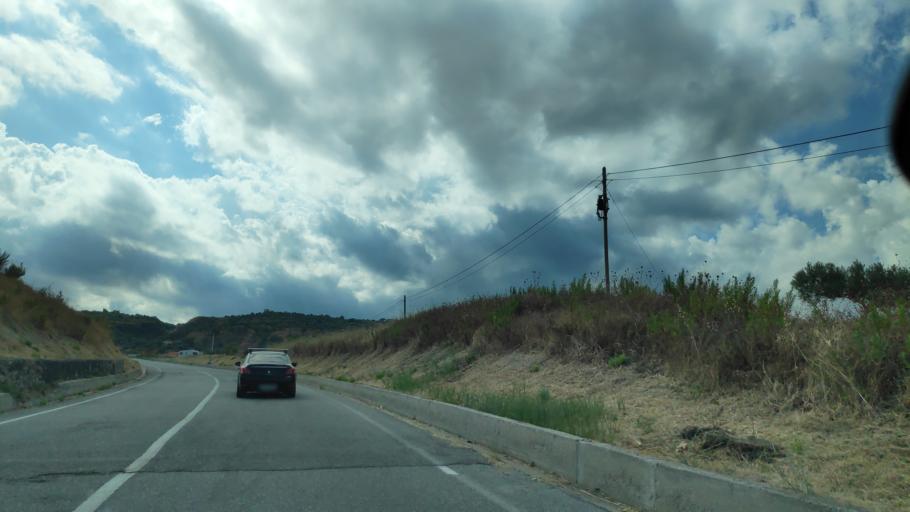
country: IT
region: Calabria
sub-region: Provincia di Catanzaro
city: Santa Caterina dello Ionio Marina
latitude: 38.5287
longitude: 16.5478
